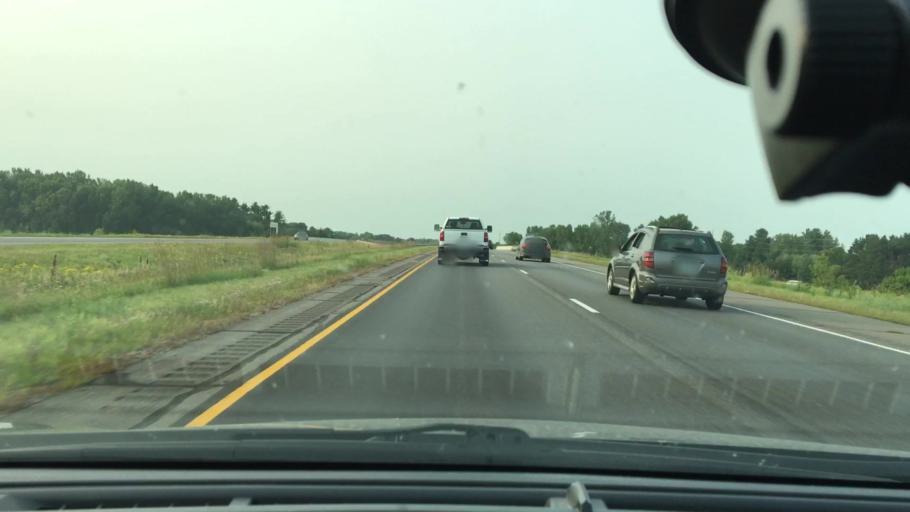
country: US
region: Minnesota
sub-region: Mille Lacs County
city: Princeton
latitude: 45.5932
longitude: -93.6009
